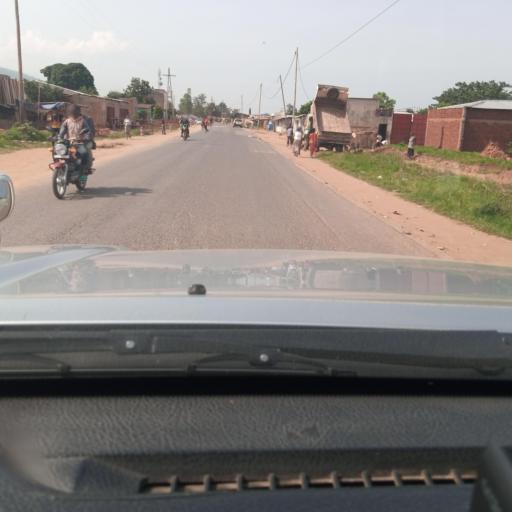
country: BI
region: Bujumbura Mairie
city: Bujumbura
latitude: -3.4676
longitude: 29.3497
